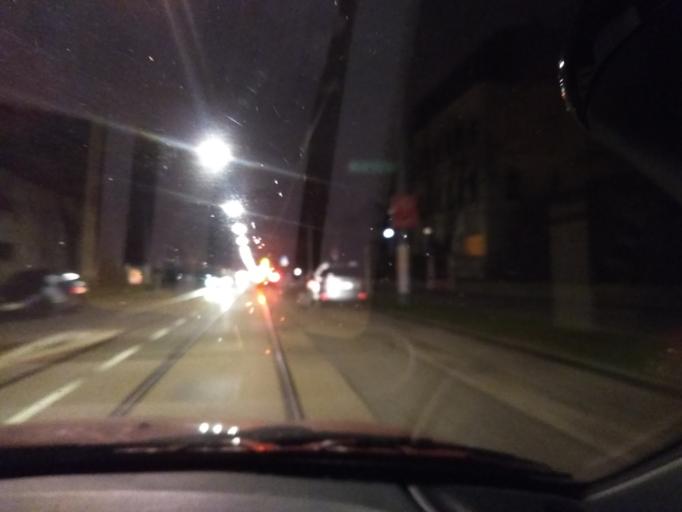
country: AT
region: Lower Austria
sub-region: Politischer Bezirk Modling
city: Perchtoldsdorf
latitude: 48.1643
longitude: 16.2807
